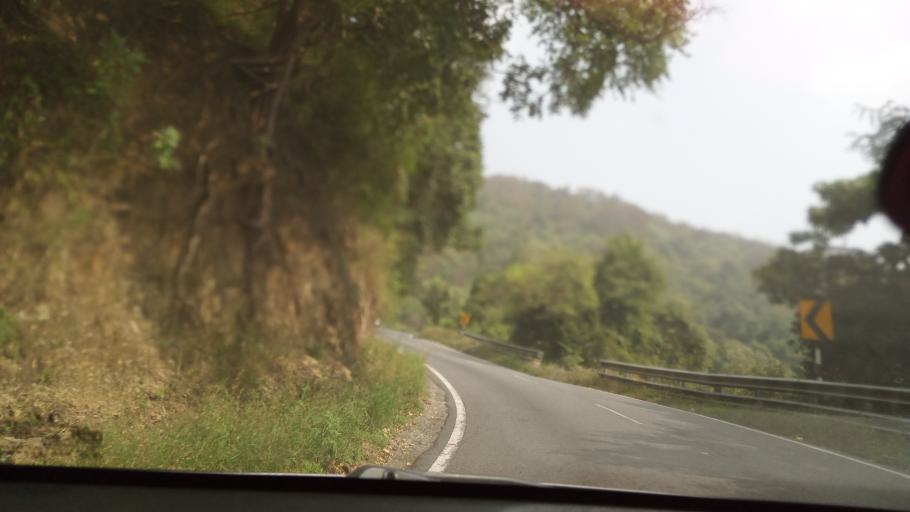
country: IN
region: Tamil Nadu
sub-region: Erode
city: Sathyamangalam
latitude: 11.6012
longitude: 77.1263
